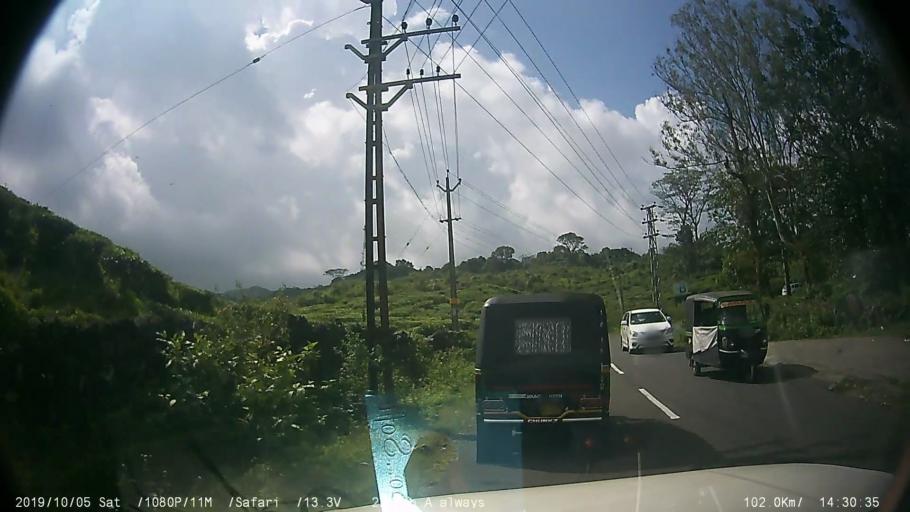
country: IN
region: Kerala
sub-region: Kottayam
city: Erattupetta
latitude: 9.6112
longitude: 76.9689
